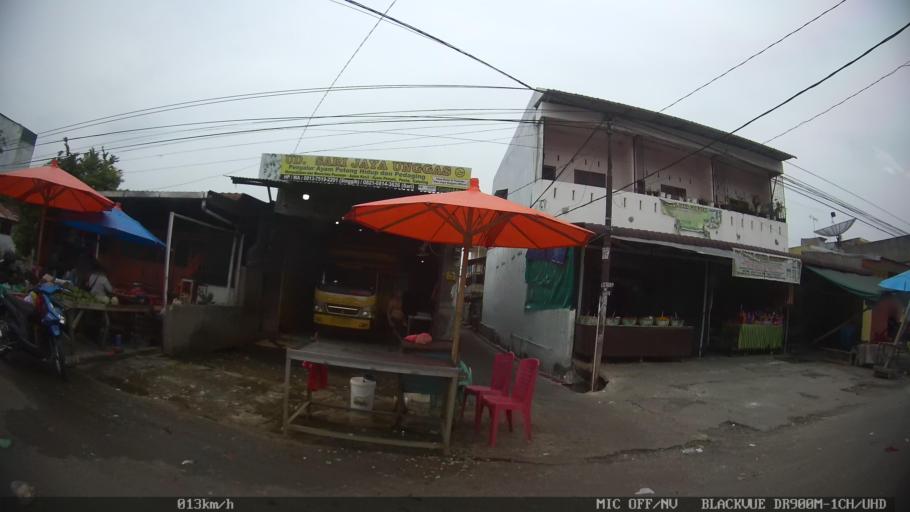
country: ID
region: North Sumatra
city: Medan
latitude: 3.5523
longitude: 98.6990
